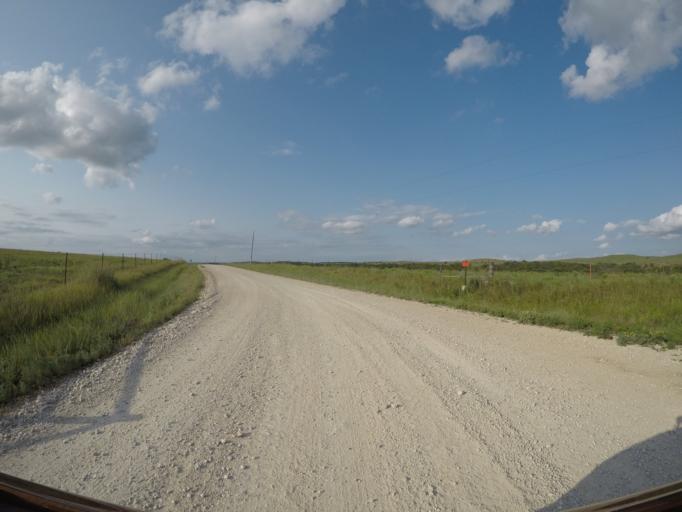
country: US
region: Kansas
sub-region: Wabaunsee County
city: Alma
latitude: 38.8718
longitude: -96.2059
